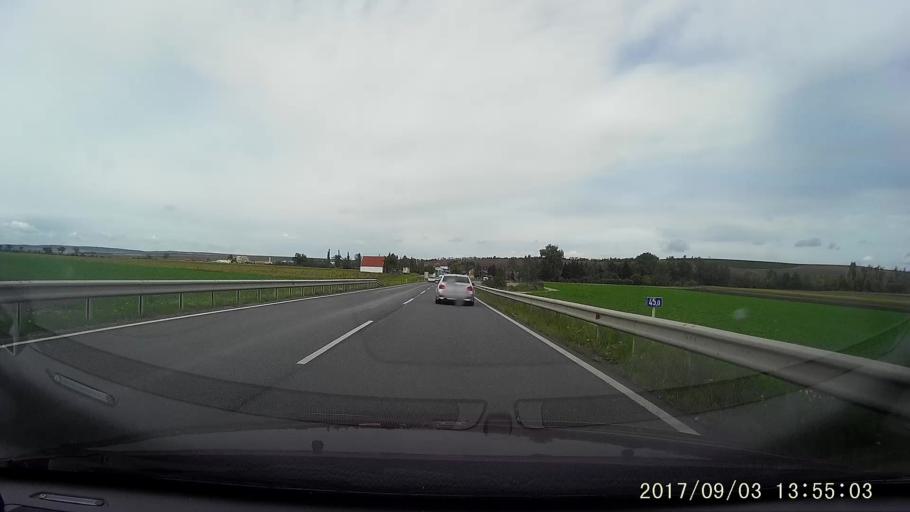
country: AT
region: Lower Austria
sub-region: Politischer Bezirk Hollabrunn
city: Haugsdorf
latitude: 48.7494
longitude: 16.0628
